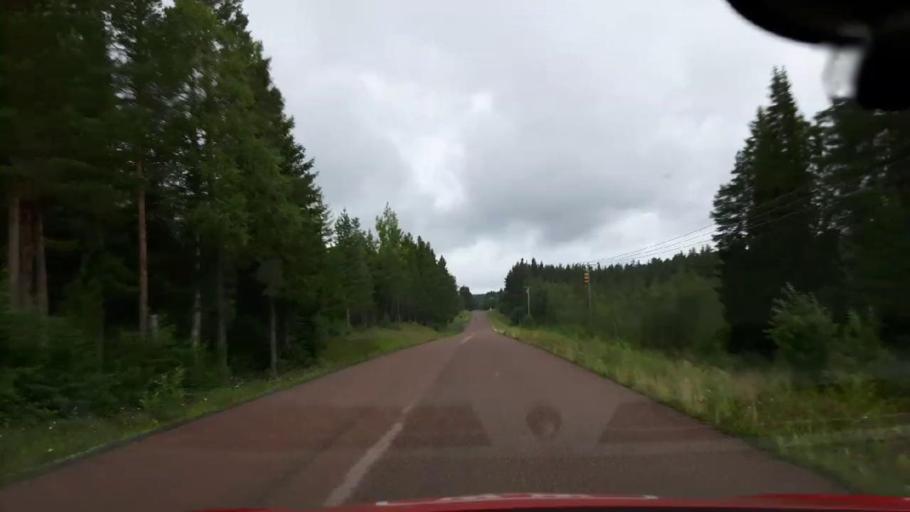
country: SE
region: Jaemtland
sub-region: Krokoms Kommun
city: Valla
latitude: 63.3401
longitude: 13.7155
